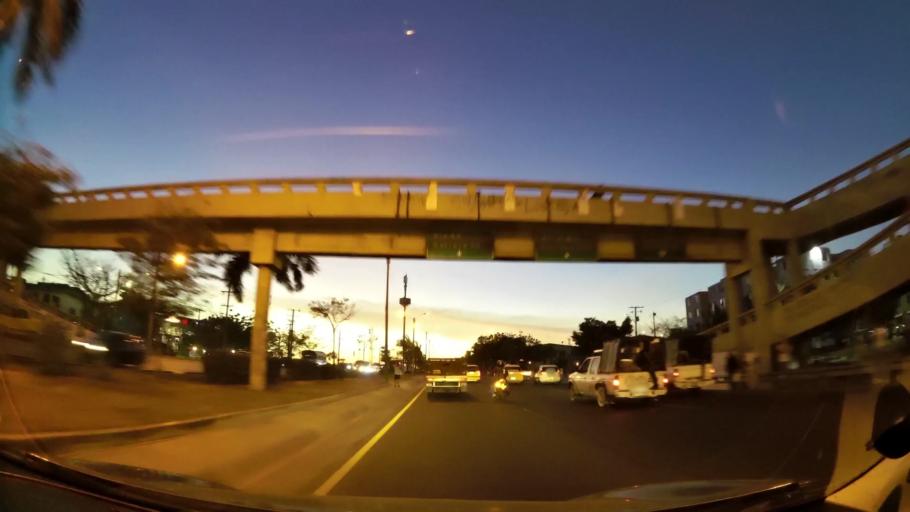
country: CO
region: Atlantico
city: Soledad
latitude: 10.9228
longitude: -74.8112
